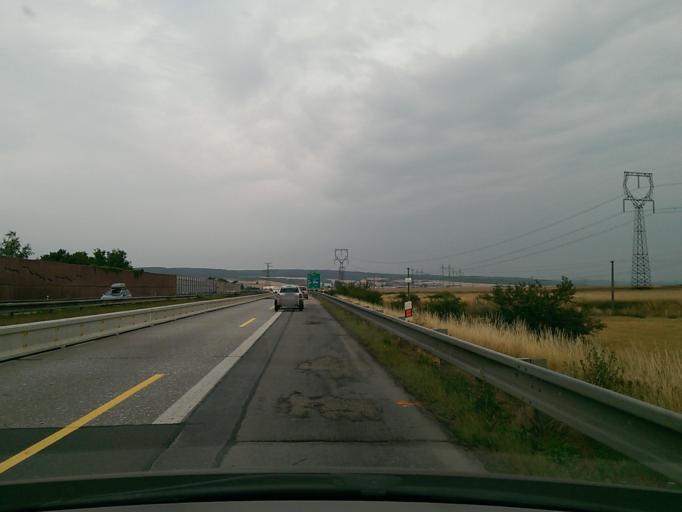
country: CZ
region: South Moravian
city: Ricany
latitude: 49.2074
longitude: 16.4187
